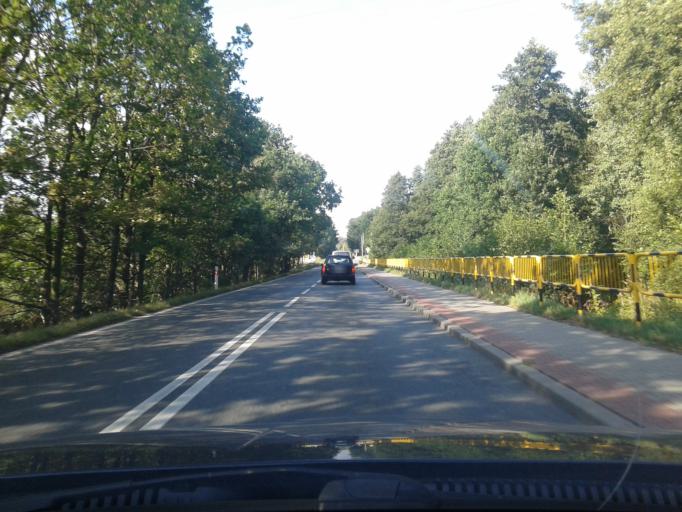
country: PL
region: Silesian Voivodeship
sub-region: Powiat wodzislawski
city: Wodzislaw Slaski
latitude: 49.9885
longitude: 18.4549
